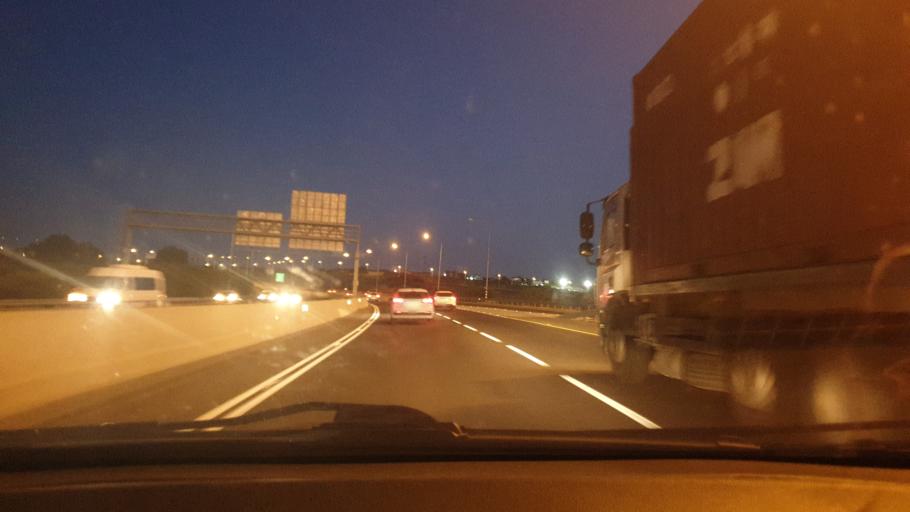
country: IL
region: Central District
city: Gedera
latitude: 31.8013
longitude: 34.7639
